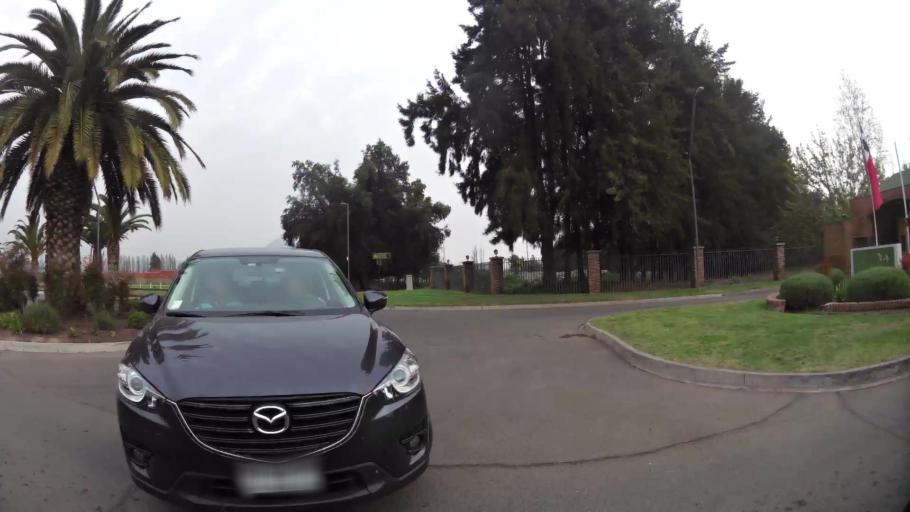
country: CL
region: Santiago Metropolitan
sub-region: Provincia de Chacabuco
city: Chicureo Abajo
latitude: -33.2762
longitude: -70.7053
